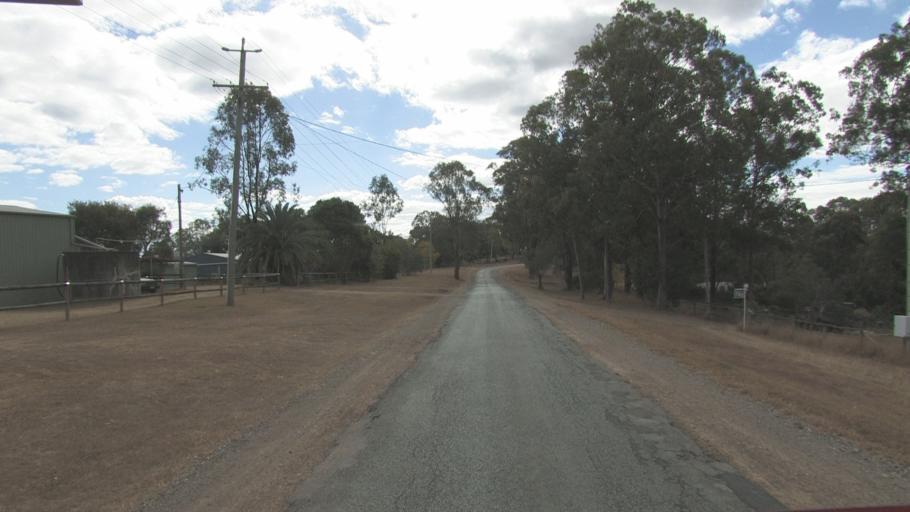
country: AU
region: Queensland
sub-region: Logan
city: Cedar Vale
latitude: -27.8860
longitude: 153.0278
